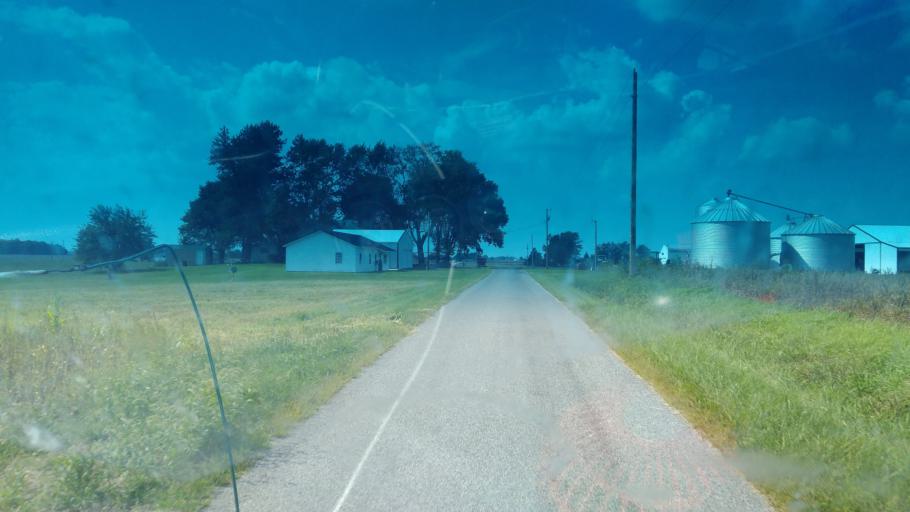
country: US
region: Ohio
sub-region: Hardin County
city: Ada
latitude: 40.6819
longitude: -83.8761
